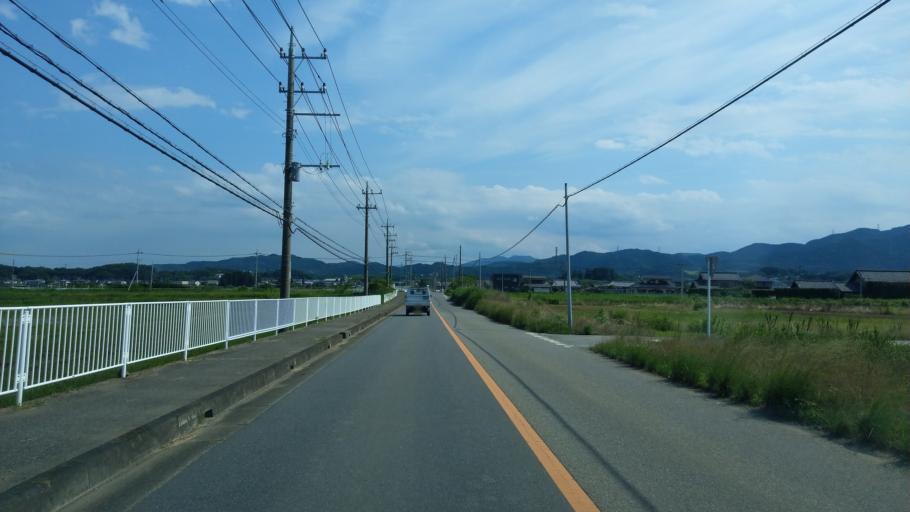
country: JP
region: Saitama
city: Kodamacho-kodamaminami
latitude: 36.1829
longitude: 139.1689
